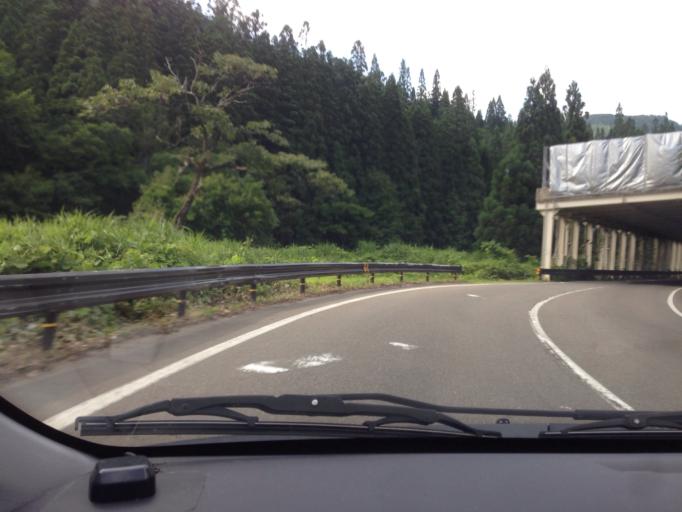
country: JP
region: Fukushima
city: Kitakata
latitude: 37.3980
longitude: 139.5481
